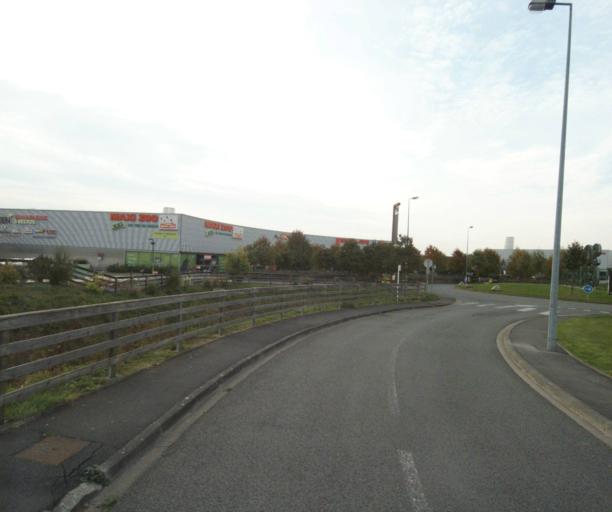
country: FR
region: Nord-Pas-de-Calais
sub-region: Departement du Nord
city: Attiches
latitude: 50.5463
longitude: 3.0531
